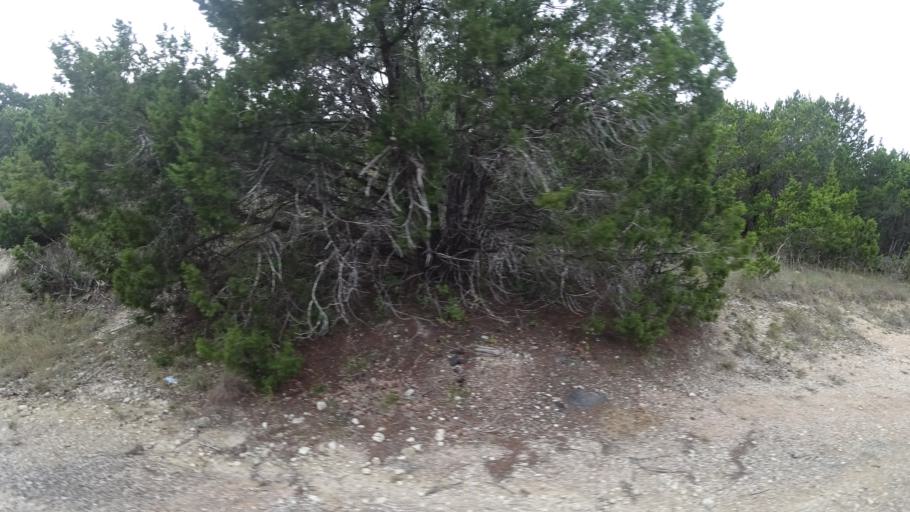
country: US
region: Texas
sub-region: Travis County
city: Hudson Bend
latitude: 30.3794
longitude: -97.9221
